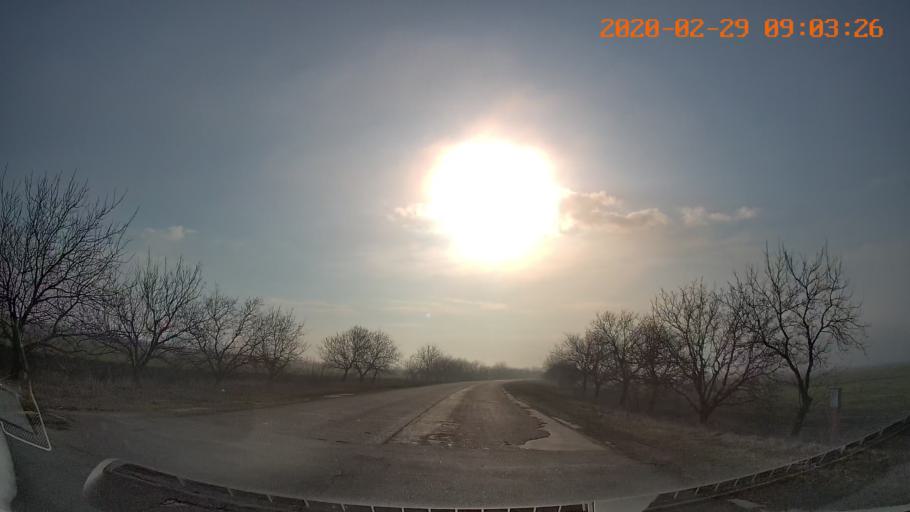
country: UA
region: Odessa
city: Velykoploske
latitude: 46.9158
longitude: 29.7286
